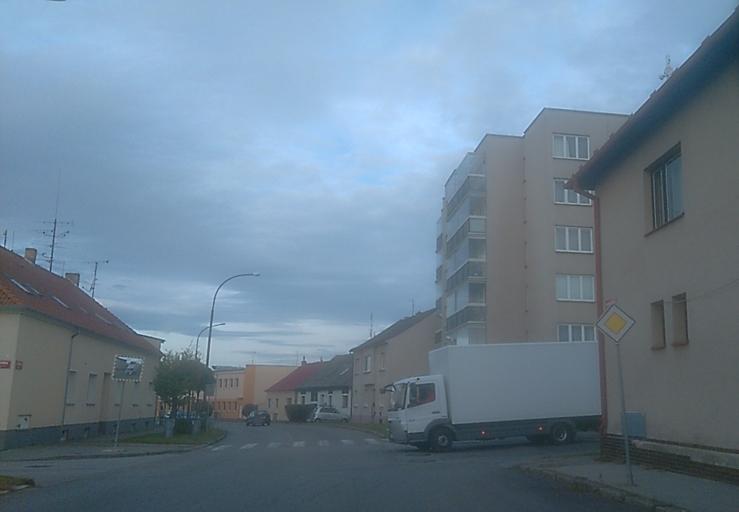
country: CZ
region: Jihocesky
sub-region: Okres Ceske Budejovice
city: Ceske Budejovice
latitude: 48.9718
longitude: 14.5088
